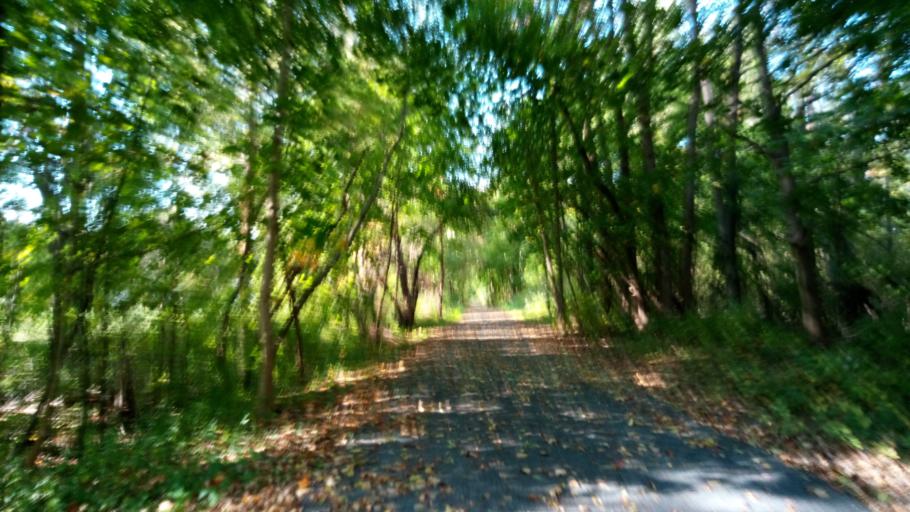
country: US
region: New York
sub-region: Wayne County
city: Clyde
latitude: 43.0754
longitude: -76.8635
